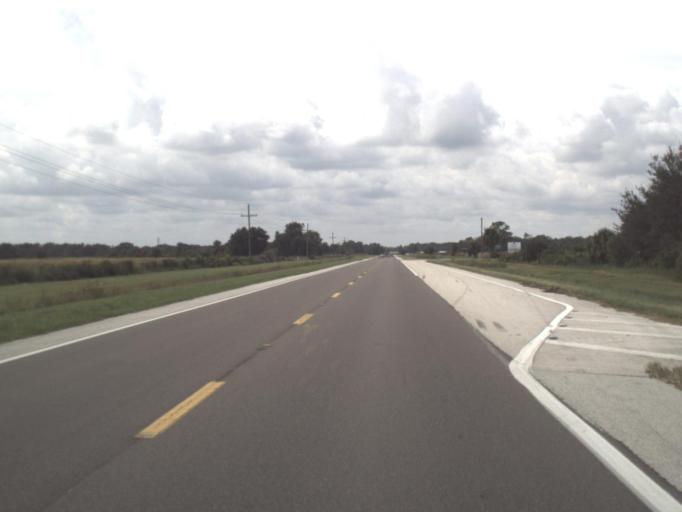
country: US
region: Florida
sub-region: Hendry County
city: LaBelle
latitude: 26.7985
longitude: -81.4249
